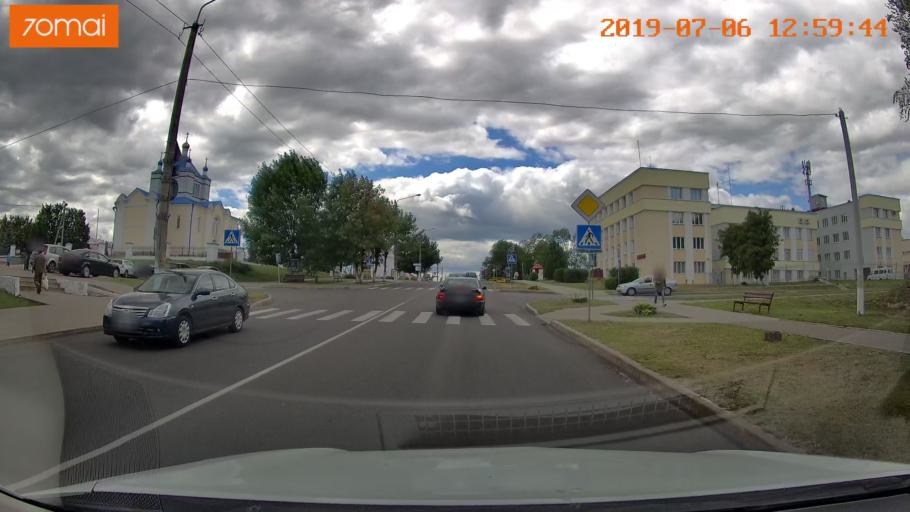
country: BY
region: Minsk
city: Dzyarzhynsk
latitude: 53.6856
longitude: 27.1335
